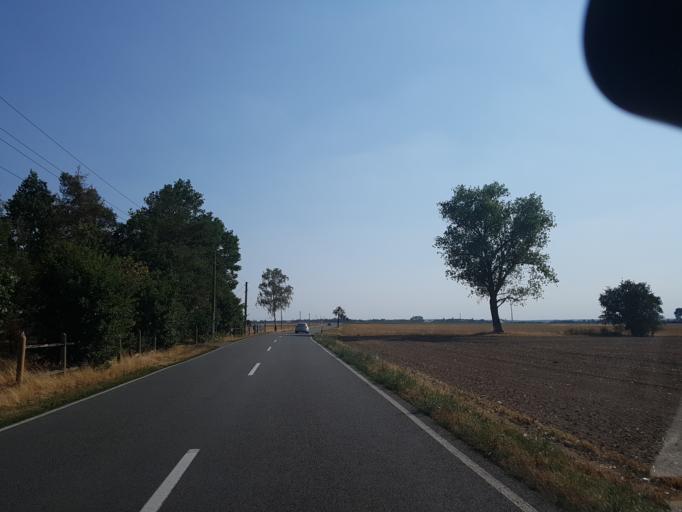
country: DE
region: Saxony-Anhalt
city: Prettin
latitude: 51.6695
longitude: 12.9935
